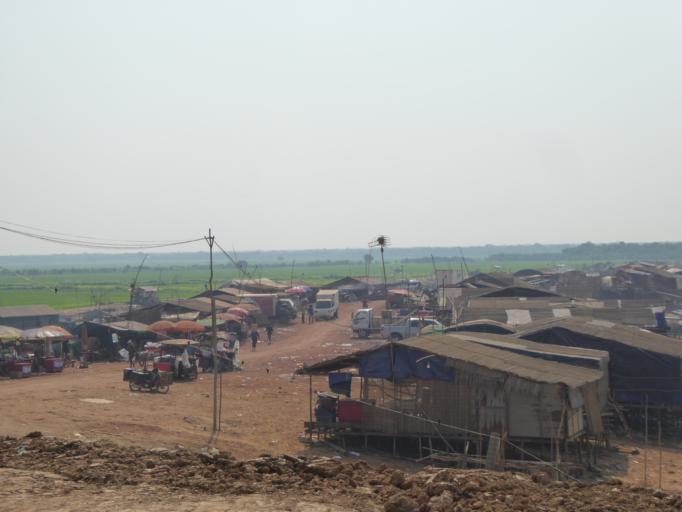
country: KH
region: Siem Reap
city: Siem Reap
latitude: 13.2645
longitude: 103.8223
